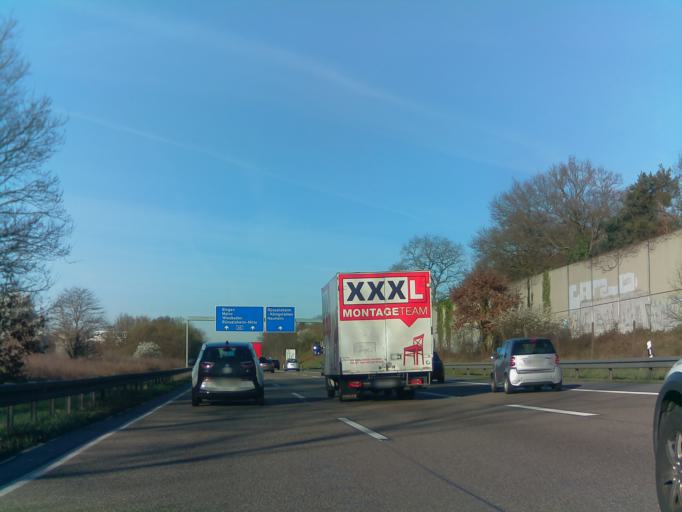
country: DE
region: Hesse
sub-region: Regierungsbezirk Darmstadt
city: Russelsheim
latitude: 49.9771
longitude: 8.4488
